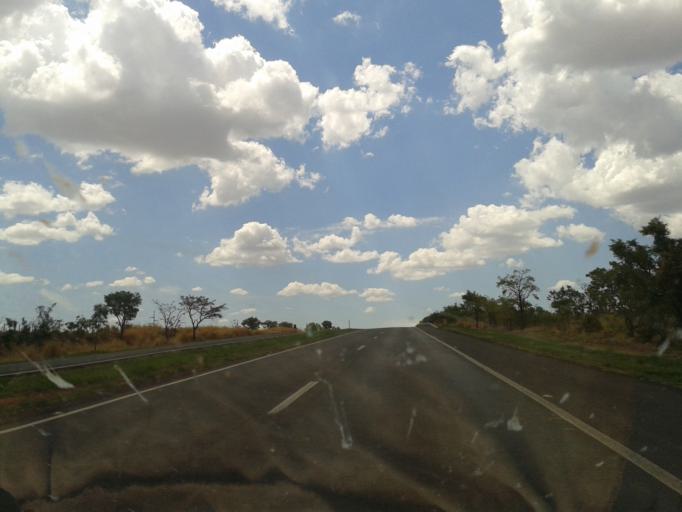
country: BR
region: Minas Gerais
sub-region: Uberlandia
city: Uberlandia
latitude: -19.1040
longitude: -48.1802
